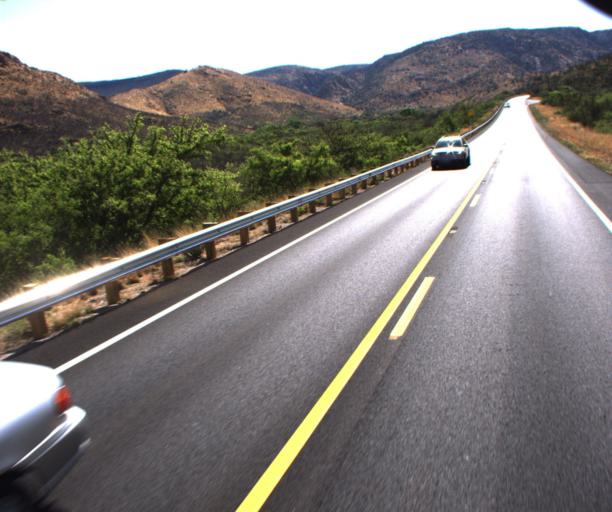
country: US
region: Arizona
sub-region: Cochise County
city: Bisbee
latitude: 31.5079
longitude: -110.0134
